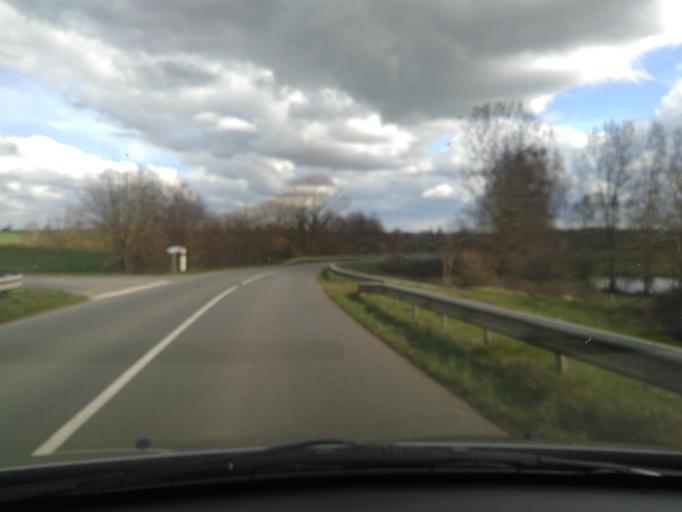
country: FR
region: Pays de la Loire
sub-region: Departement de la Vendee
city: Saint-Martin-des-Noyers
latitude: 46.7102
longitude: -1.1561
